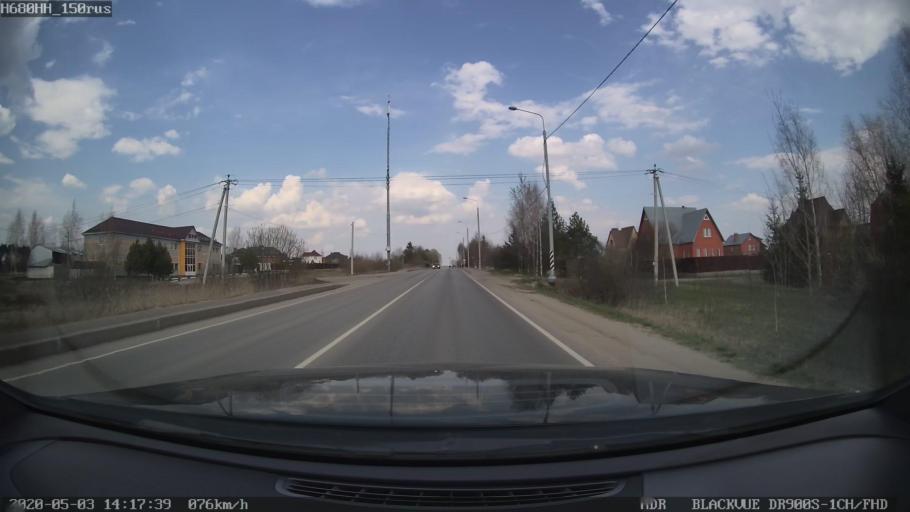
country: RU
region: Moskovskaya
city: Solnechnogorsk
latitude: 56.2107
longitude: 36.9669
